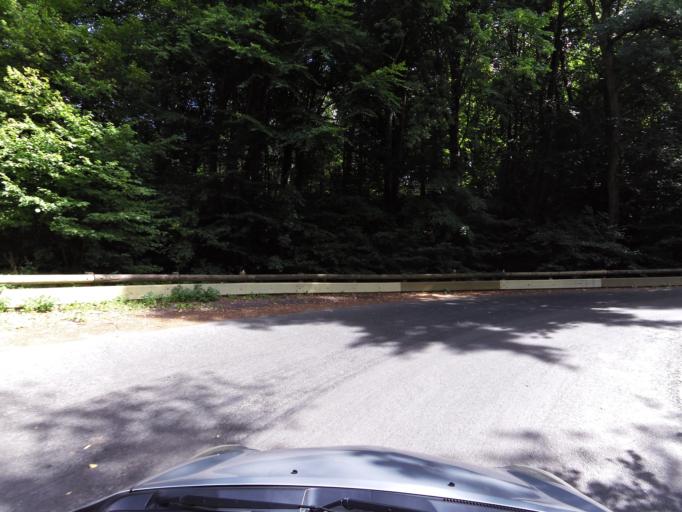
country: FR
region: Picardie
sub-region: Departement de l'Aisne
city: Bruyeres-et-Montberault
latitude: 49.5044
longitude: 3.6306
